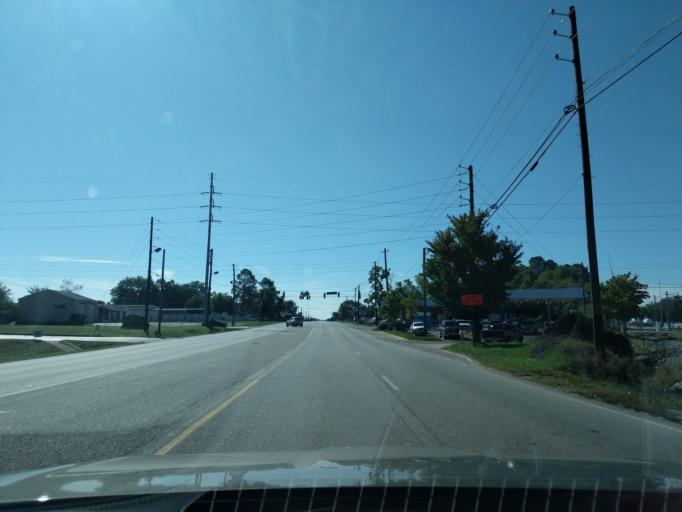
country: US
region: Georgia
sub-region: Richmond County
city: Augusta
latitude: 33.4178
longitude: -82.0071
